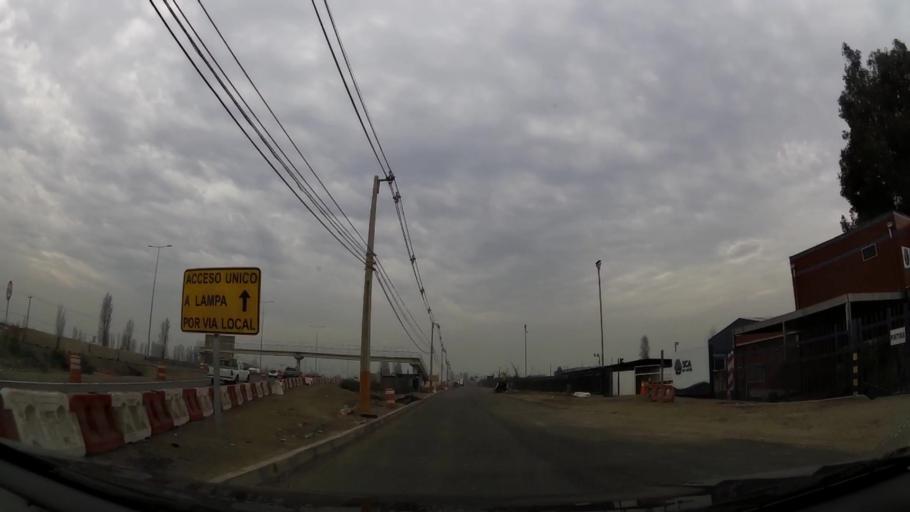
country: CL
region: Santiago Metropolitan
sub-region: Provincia de Chacabuco
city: Chicureo Abajo
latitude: -33.2626
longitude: -70.7472
